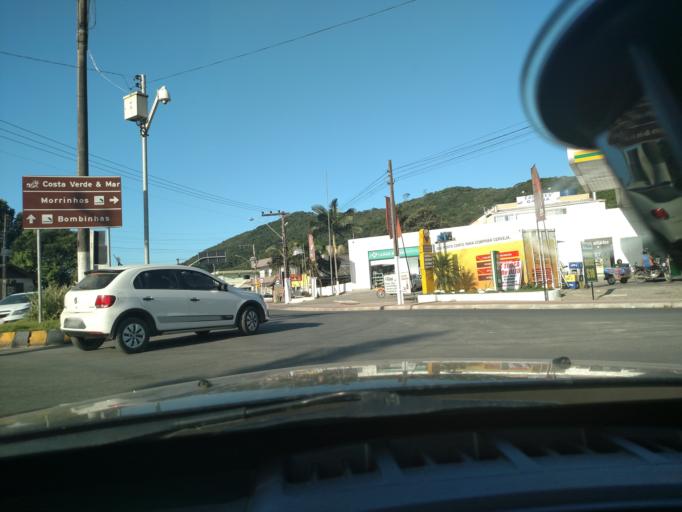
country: BR
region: Santa Catarina
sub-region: Porto Belo
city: Porto Belo
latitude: -27.1704
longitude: -48.5236
